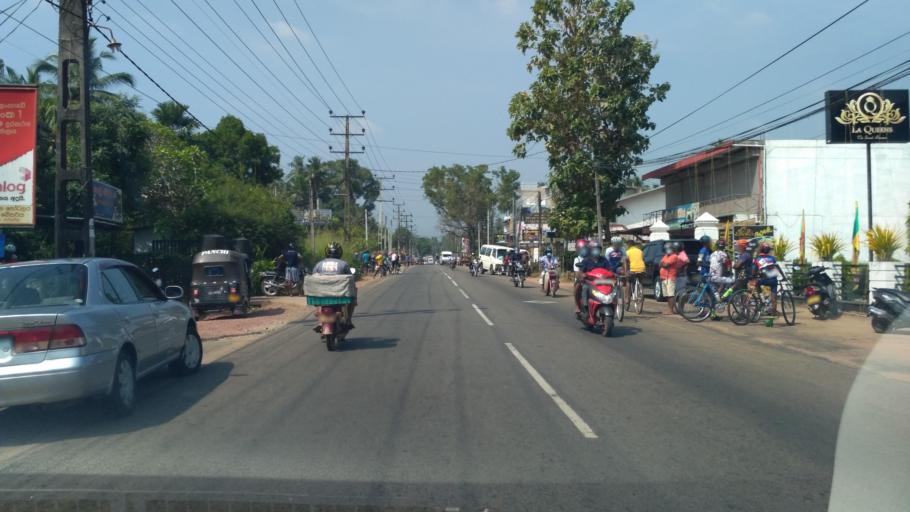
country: LK
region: Western
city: Minuwangoda
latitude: 7.3200
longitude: 79.9700
